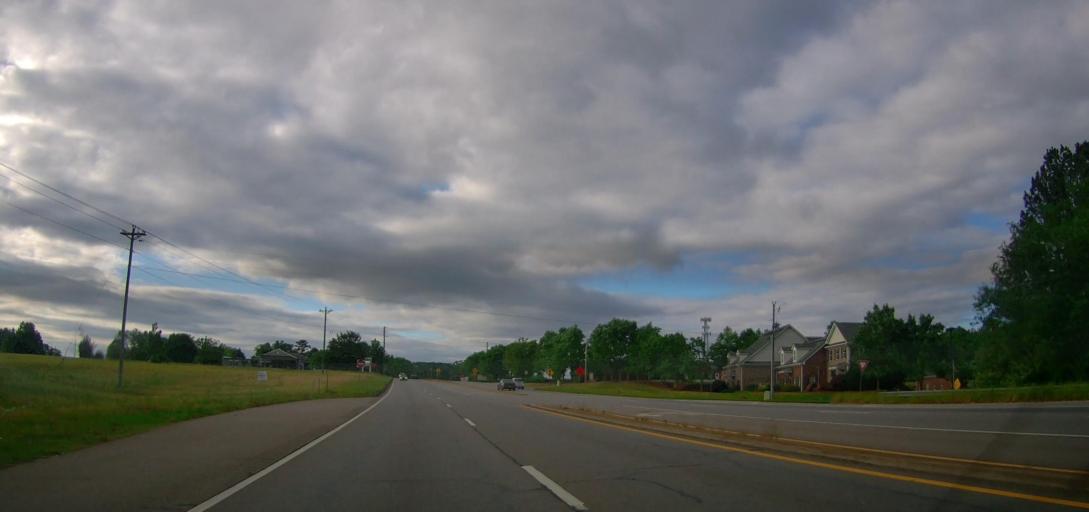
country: US
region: Georgia
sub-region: Oconee County
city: Watkinsville
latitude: 33.8855
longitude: -83.4134
